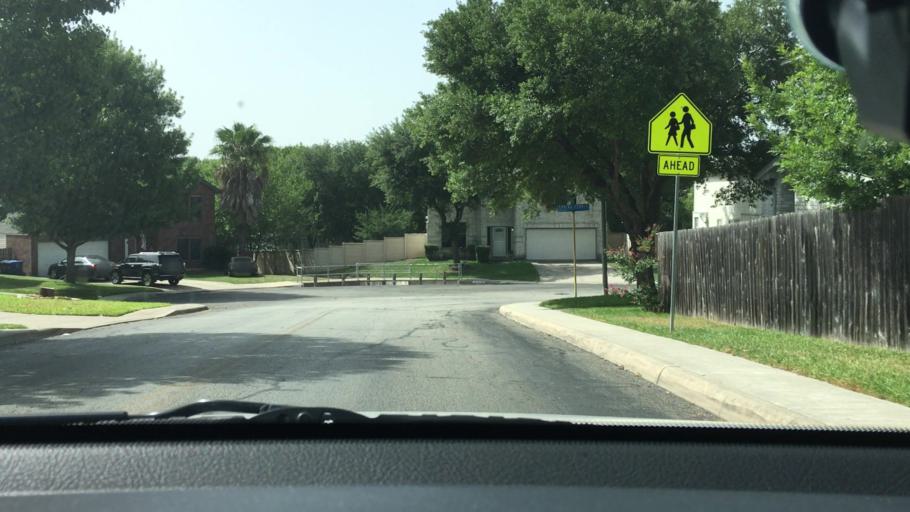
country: US
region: Texas
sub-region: Bexar County
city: Live Oak
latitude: 29.5799
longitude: -98.3843
